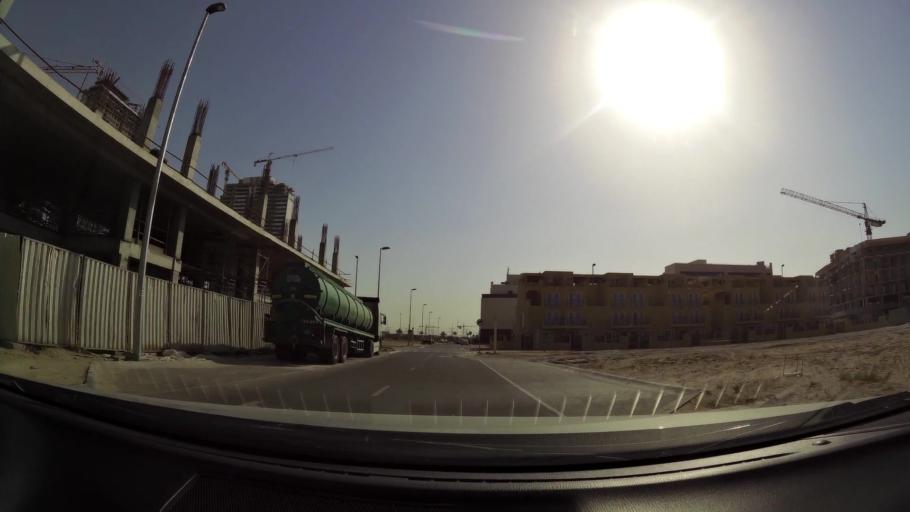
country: AE
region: Dubai
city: Dubai
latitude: 25.0557
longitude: 55.2002
